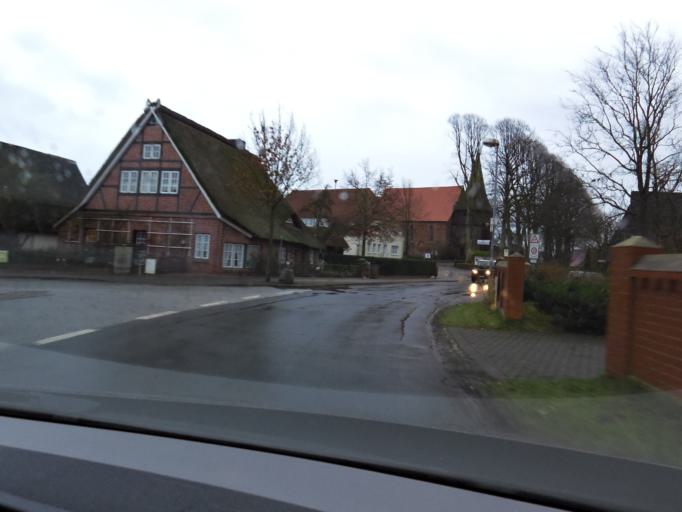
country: DE
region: Schleswig-Holstein
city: Mustin
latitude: 53.6871
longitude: 10.8850
